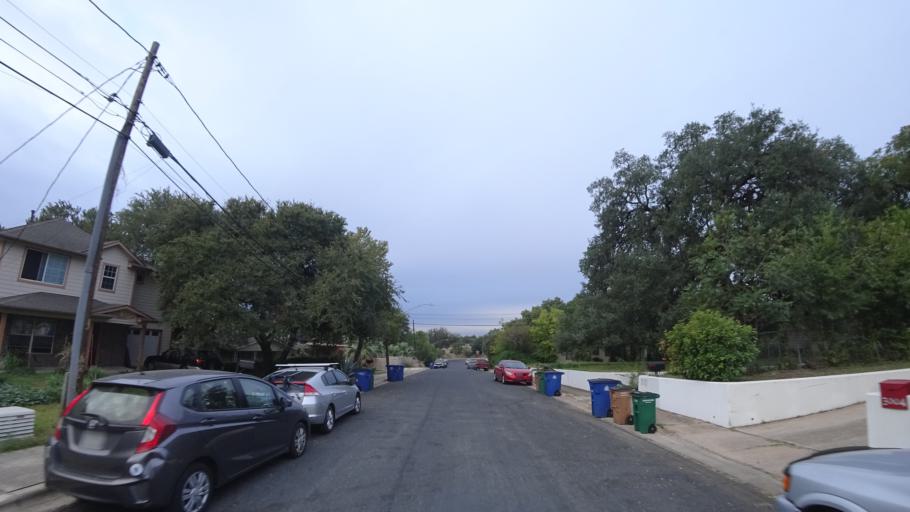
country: US
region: Texas
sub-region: Travis County
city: Austin
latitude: 30.2672
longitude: -97.7091
